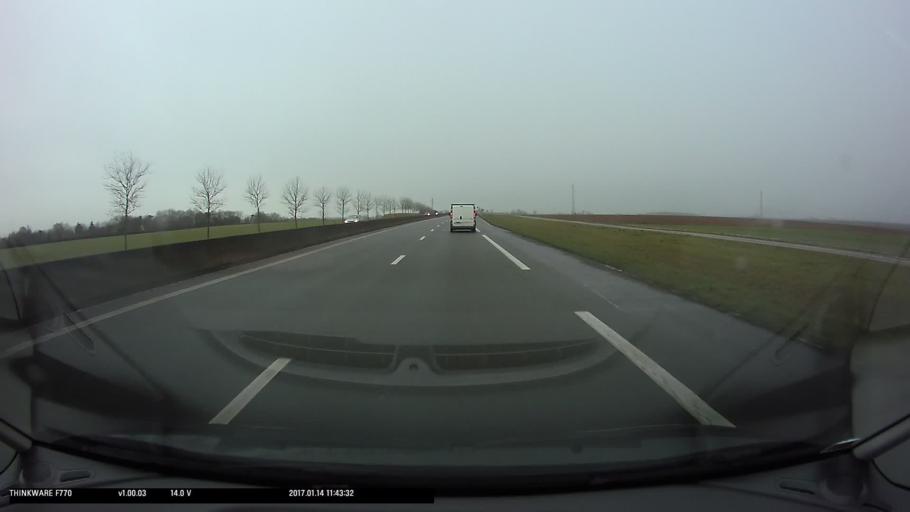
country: FR
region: Ile-de-France
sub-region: Departement du Val-d'Oise
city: Vigny
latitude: 49.0784
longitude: 1.9422
